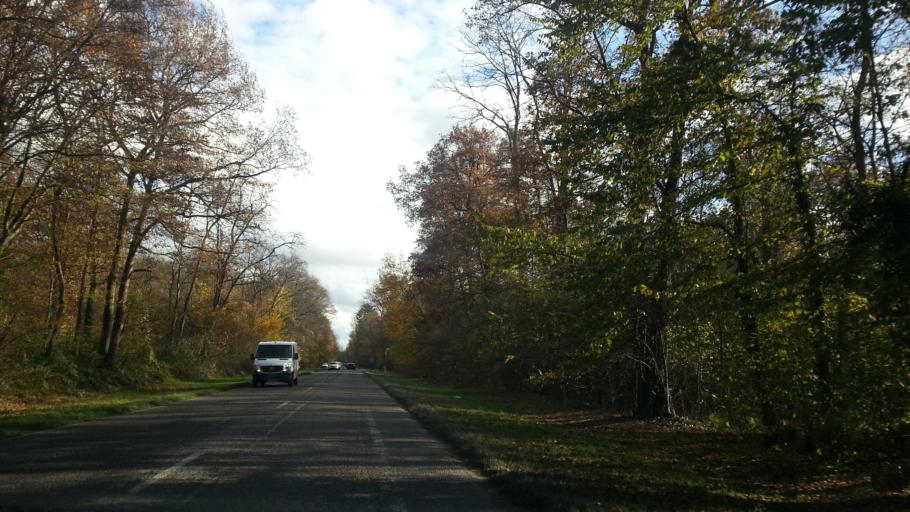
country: FR
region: Picardie
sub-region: Departement de l'Oise
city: Saint-Maximin
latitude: 49.2096
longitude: 2.4489
